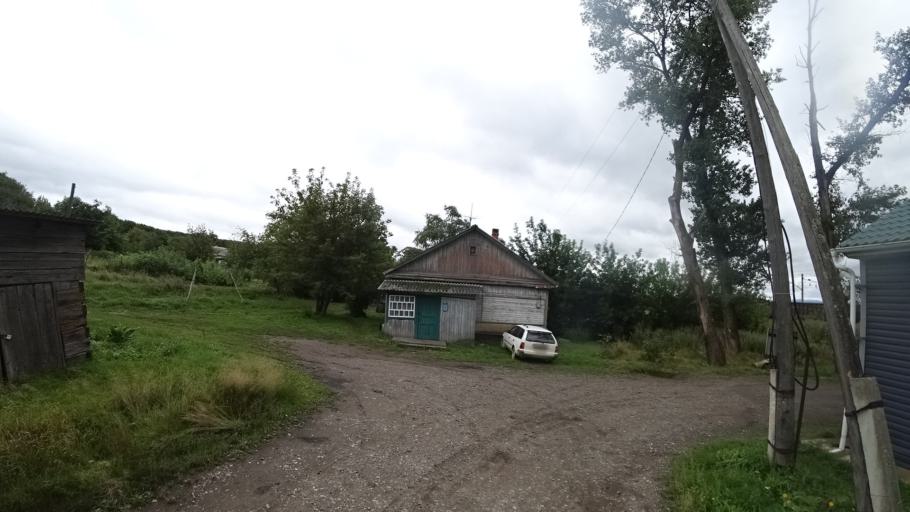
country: RU
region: Primorskiy
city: Chernigovka
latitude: 44.4418
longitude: 132.5719
